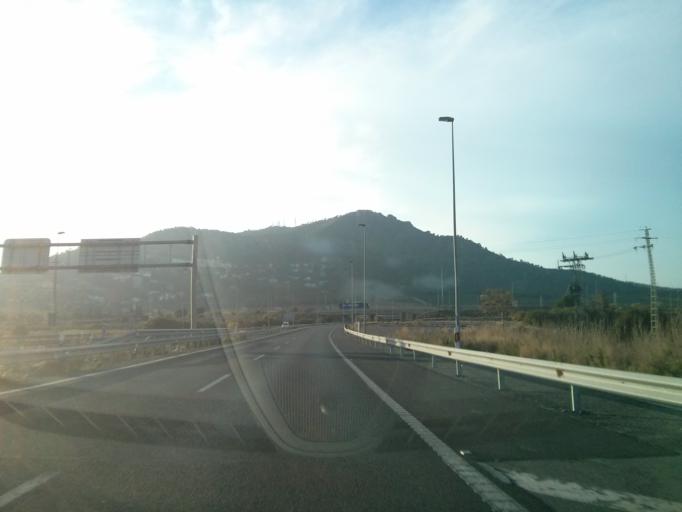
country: ES
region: Valencia
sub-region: Provincia de Valencia
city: Pucol
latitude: 39.6299
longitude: -0.3011
